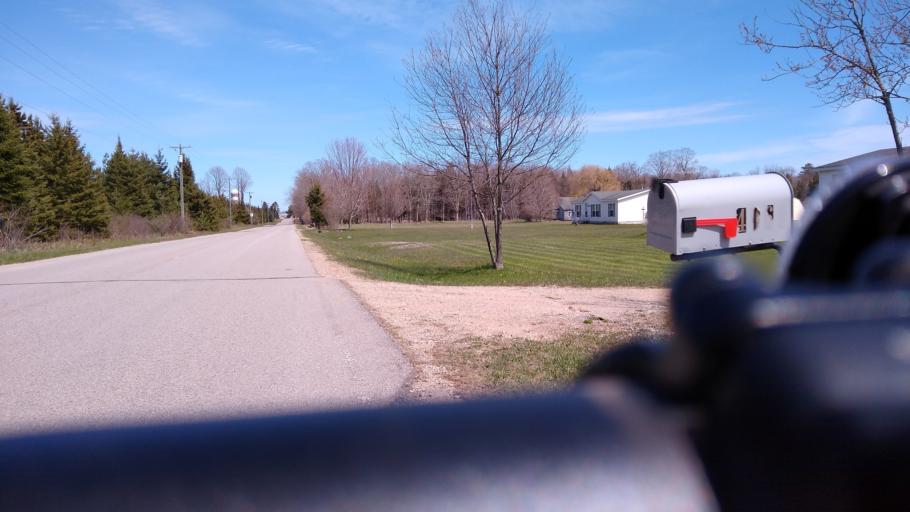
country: US
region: Michigan
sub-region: Delta County
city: Escanaba
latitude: 45.6955
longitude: -87.1611
